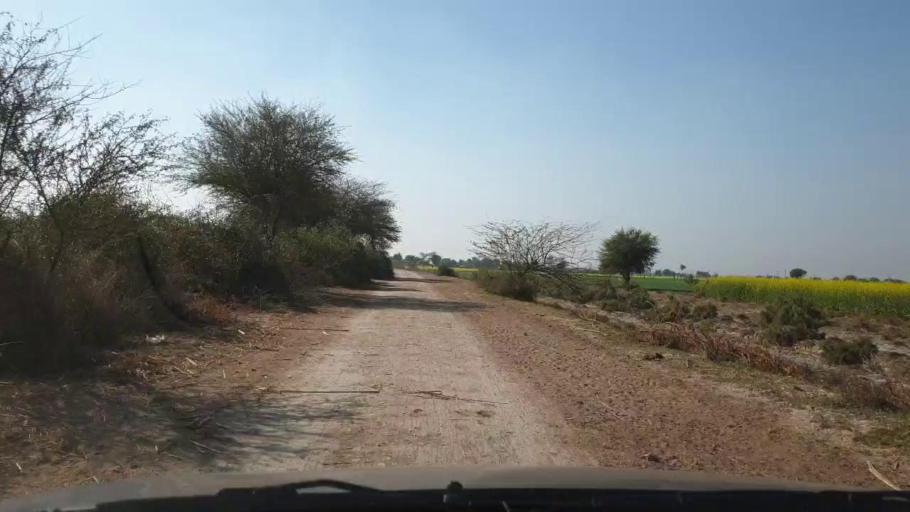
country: PK
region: Sindh
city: Jhol
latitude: 25.9265
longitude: 68.7964
